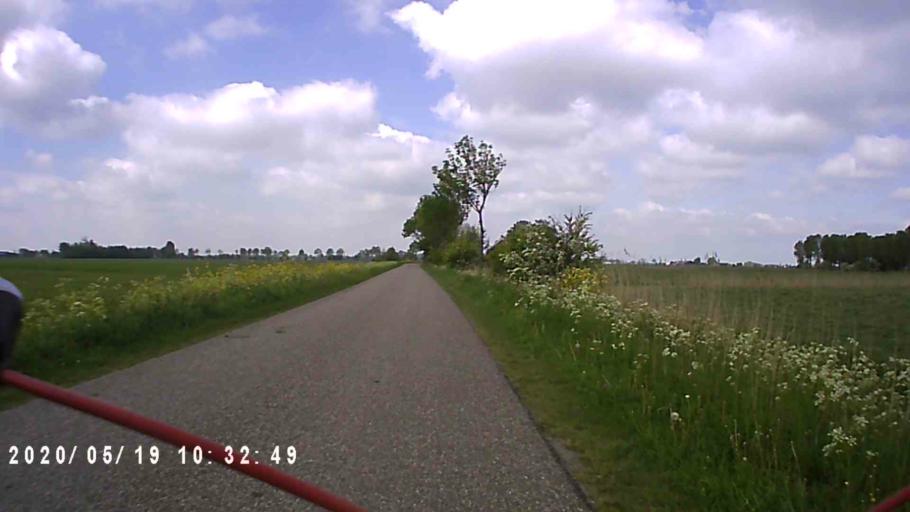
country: NL
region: Friesland
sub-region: Gemeente Kollumerland en Nieuwkruisland
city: Kollum
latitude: 53.2882
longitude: 6.1916
